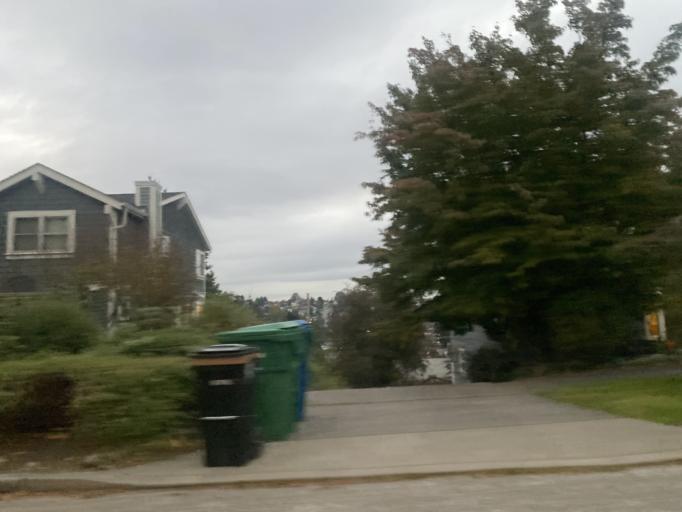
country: US
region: Washington
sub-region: King County
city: Seattle
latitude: 47.6432
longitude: -122.4050
